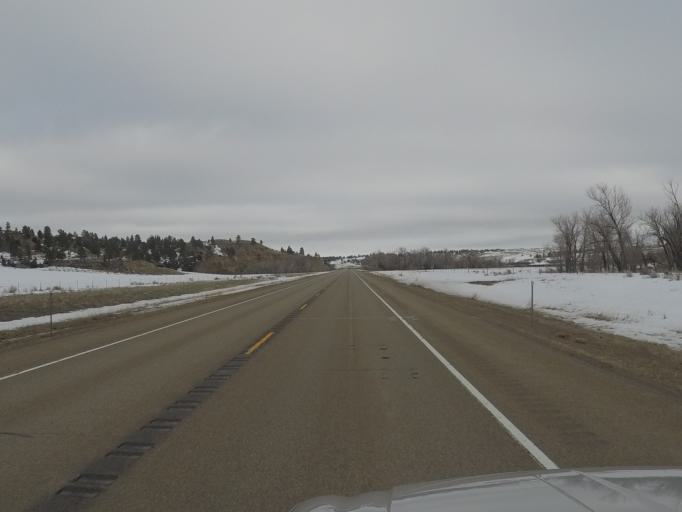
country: US
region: Montana
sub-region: Golden Valley County
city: Ryegate
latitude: 46.3077
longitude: -109.1219
